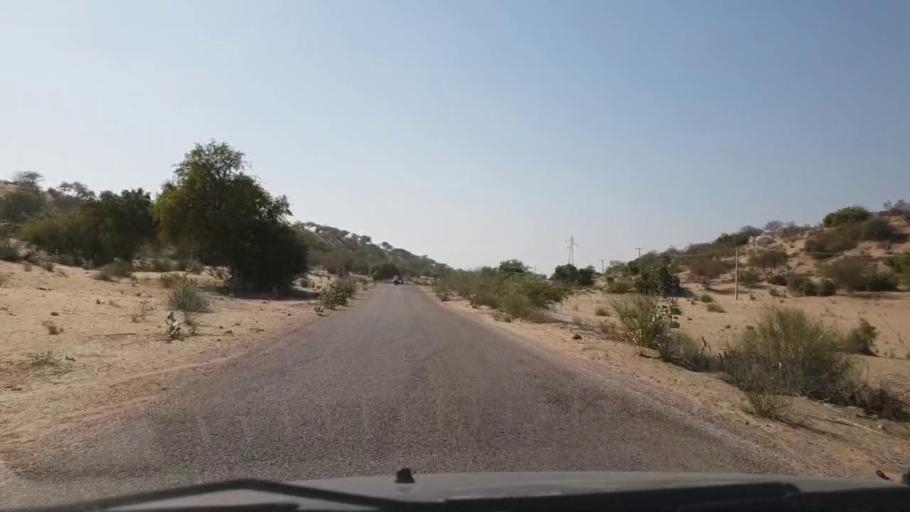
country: PK
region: Sindh
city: Diplo
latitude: 24.5777
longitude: 69.6959
